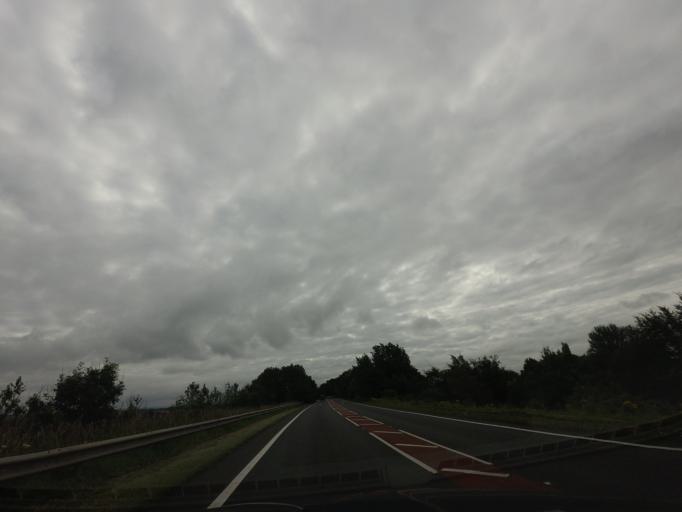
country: GB
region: Scotland
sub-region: Dumfries and Galloway
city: Gretna
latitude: 54.9929
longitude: -3.1179
